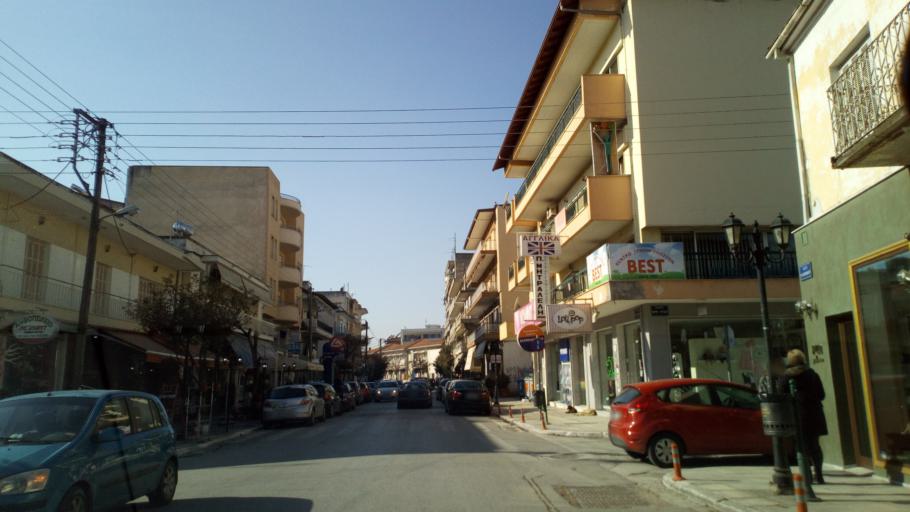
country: GR
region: Central Macedonia
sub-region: Nomos Thessalonikis
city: Lagkadas
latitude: 40.7502
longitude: 23.0658
